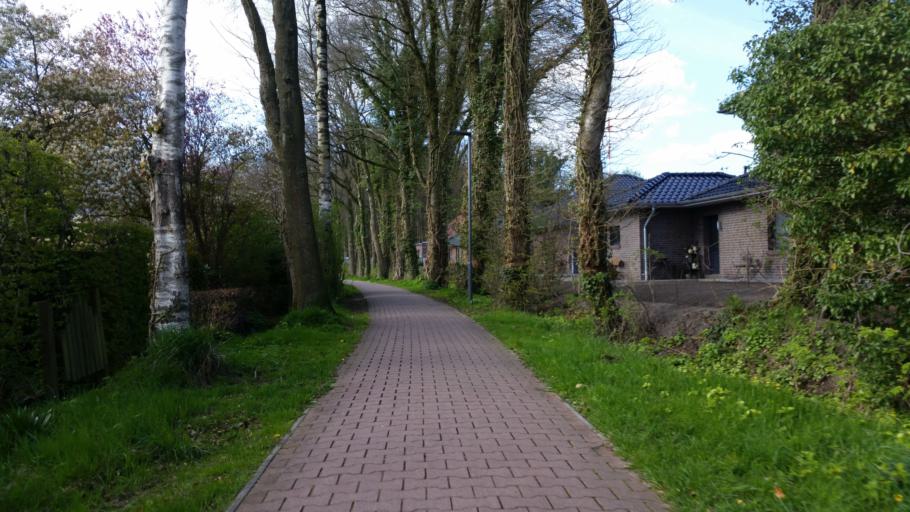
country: DE
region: Lower Saxony
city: Aurich
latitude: 53.4556
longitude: 7.5071
